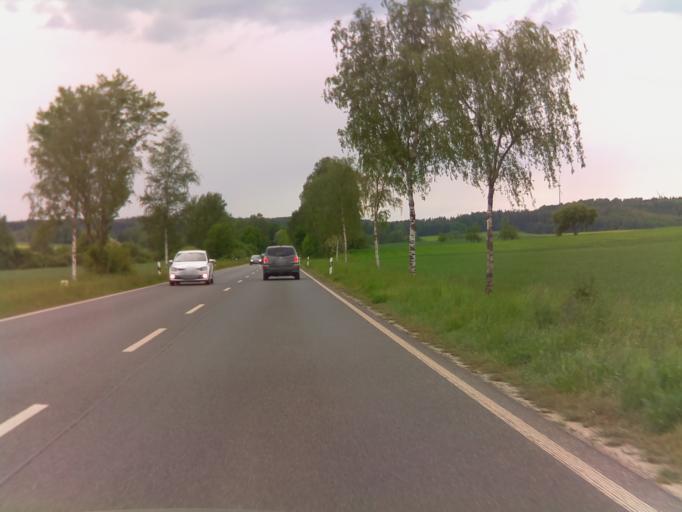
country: DE
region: Hesse
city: Neustadt (Hessen)
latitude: 50.8464
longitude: 9.0903
